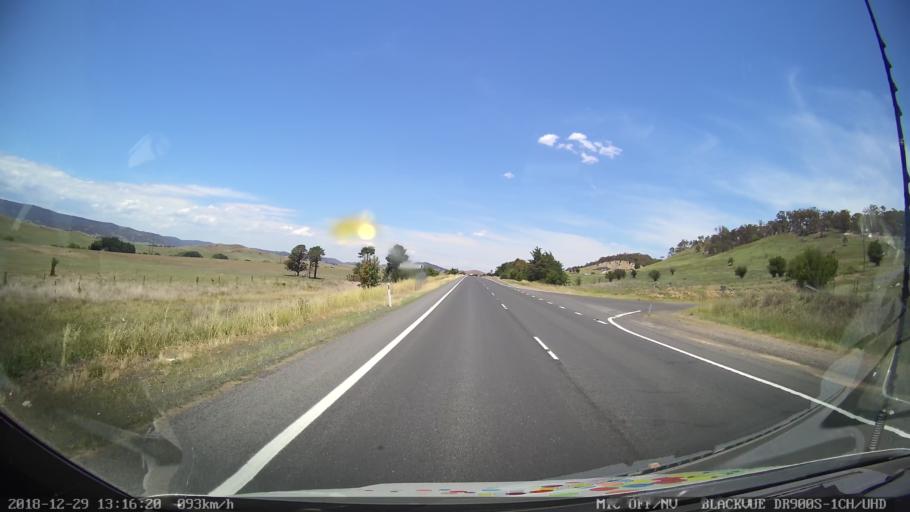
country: AU
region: Australian Capital Territory
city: Macarthur
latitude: -35.7219
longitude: 149.1589
